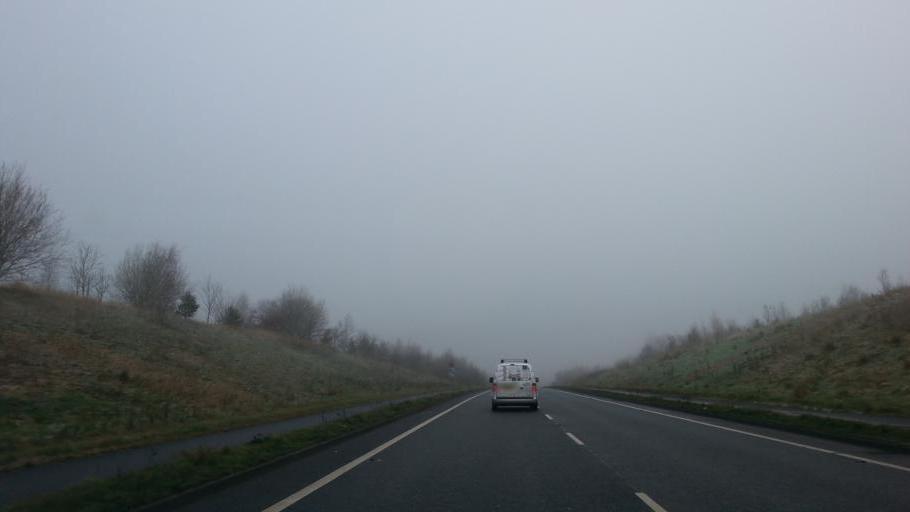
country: GB
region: England
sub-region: Cheshire East
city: Alderley Edge
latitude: 53.3002
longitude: -2.2498
